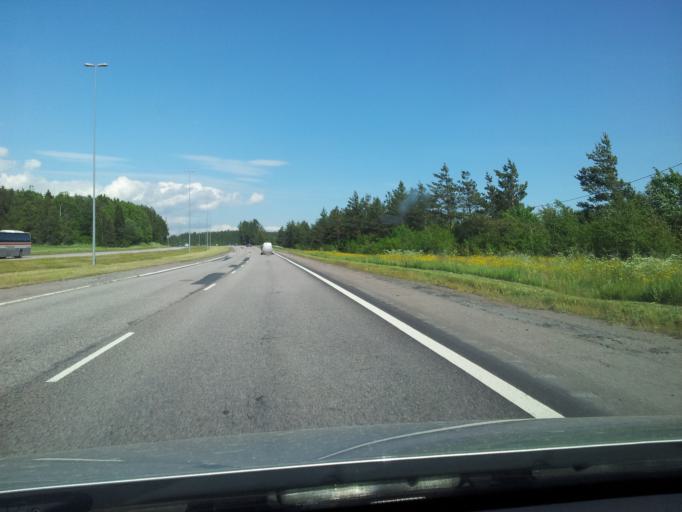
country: FI
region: Uusimaa
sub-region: Porvoo
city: Porvoo
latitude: 60.3582
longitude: 25.5372
